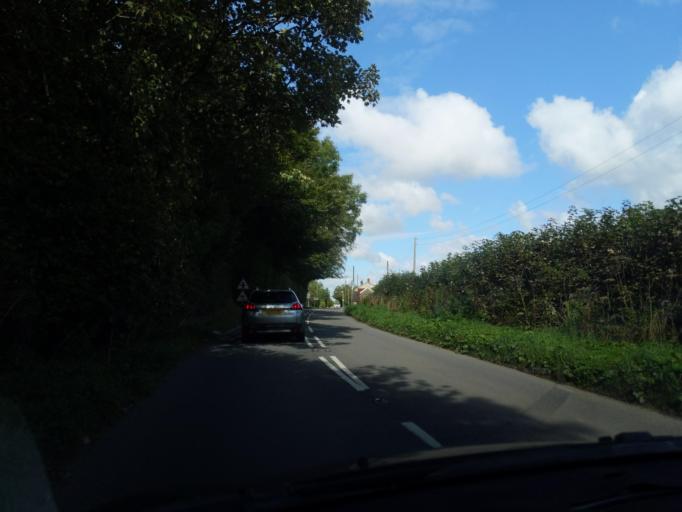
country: GB
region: England
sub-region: Devon
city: Holsworthy
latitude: 50.8495
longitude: -4.3348
